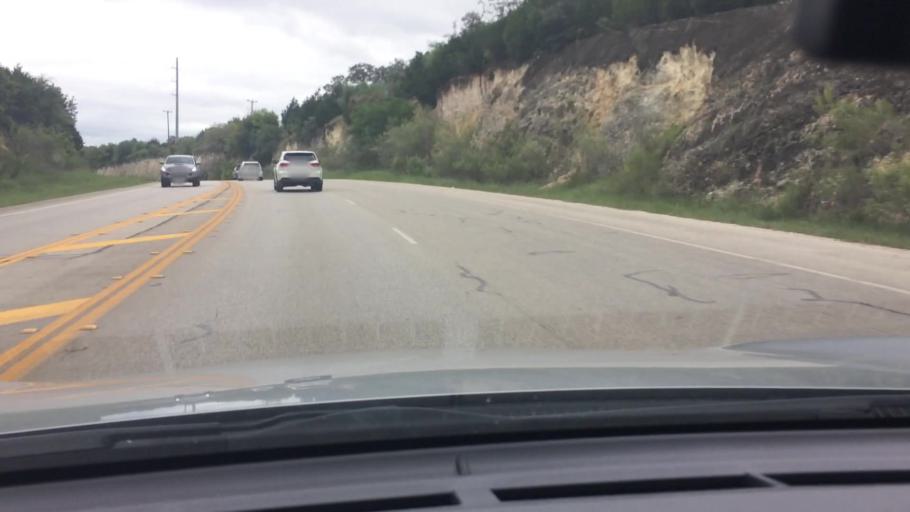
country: US
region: Texas
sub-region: Bexar County
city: Live Oak
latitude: 29.6089
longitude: -98.3685
